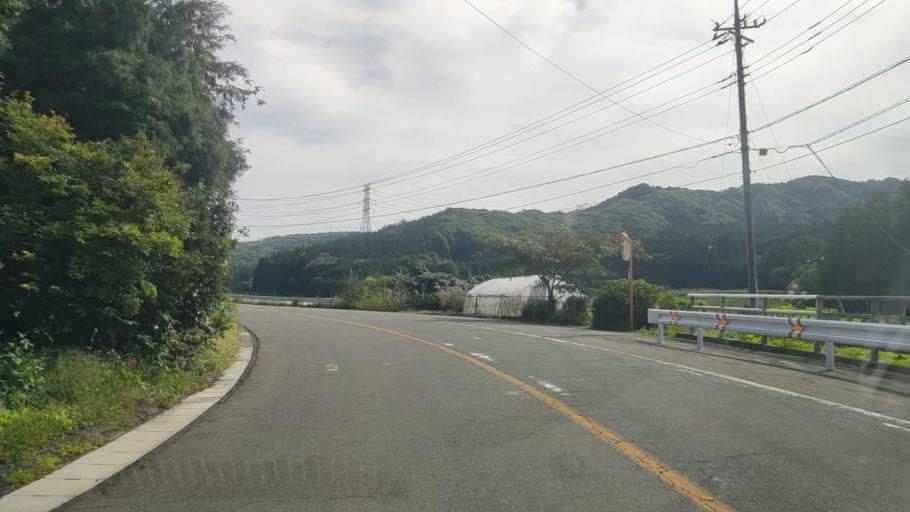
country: JP
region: Gunma
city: Numata
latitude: 36.6275
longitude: 138.9716
